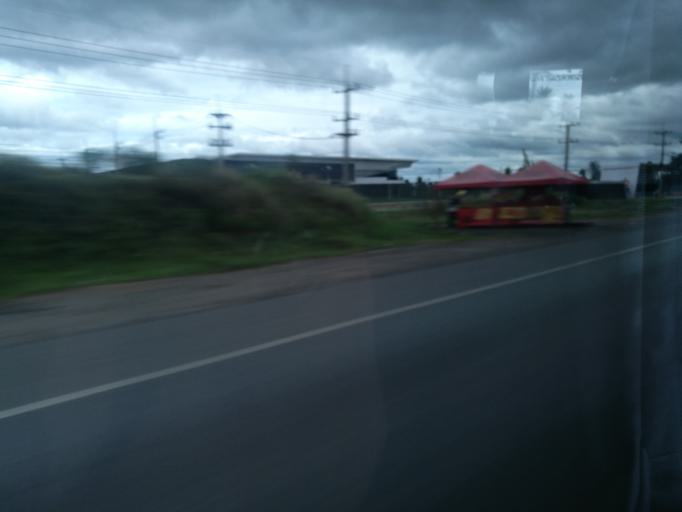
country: TH
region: Prachuap Khiri Khan
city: Sam Roi Yot
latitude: 12.1879
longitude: 99.8510
